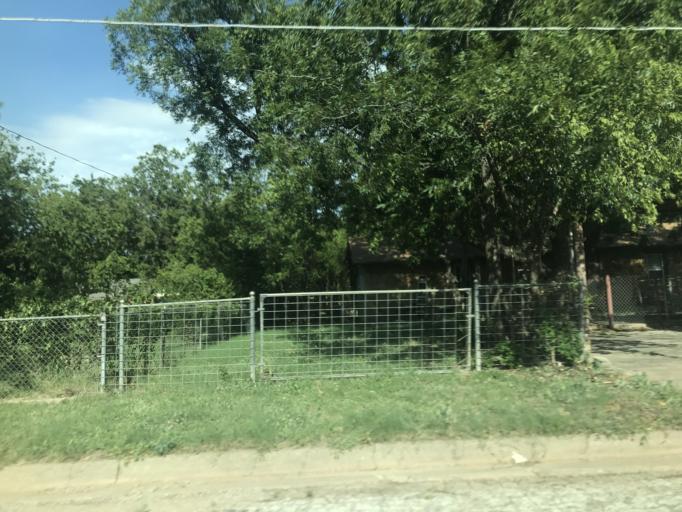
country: US
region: Texas
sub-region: Taylor County
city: Abilene
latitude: 32.4432
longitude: -99.7645
